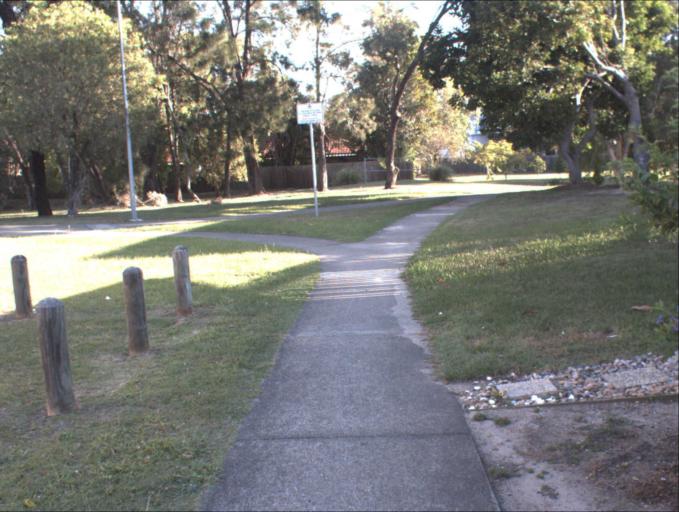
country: AU
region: Queensland
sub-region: Logan
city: Springwood
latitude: -27.6077
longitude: 153.1237
